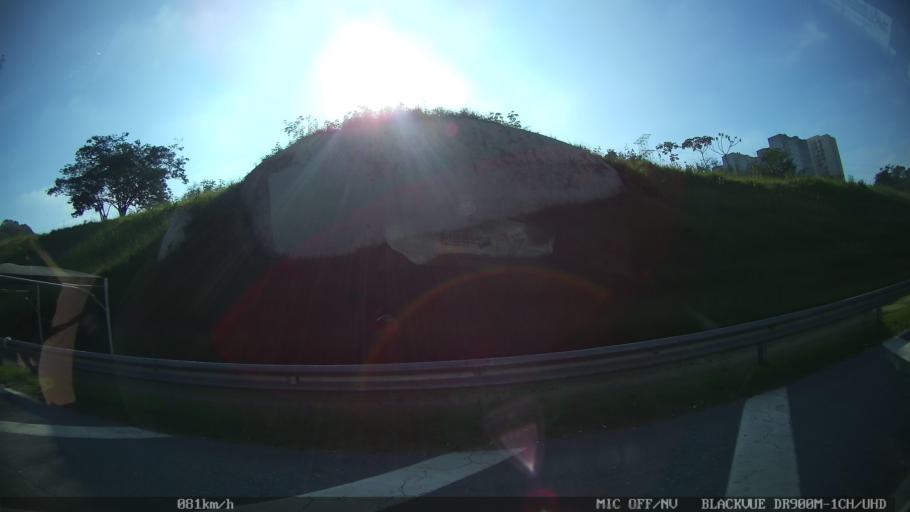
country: BR
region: Sao Paulo
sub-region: Osasco
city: Osasco
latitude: -23.5010
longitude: -46.7262
